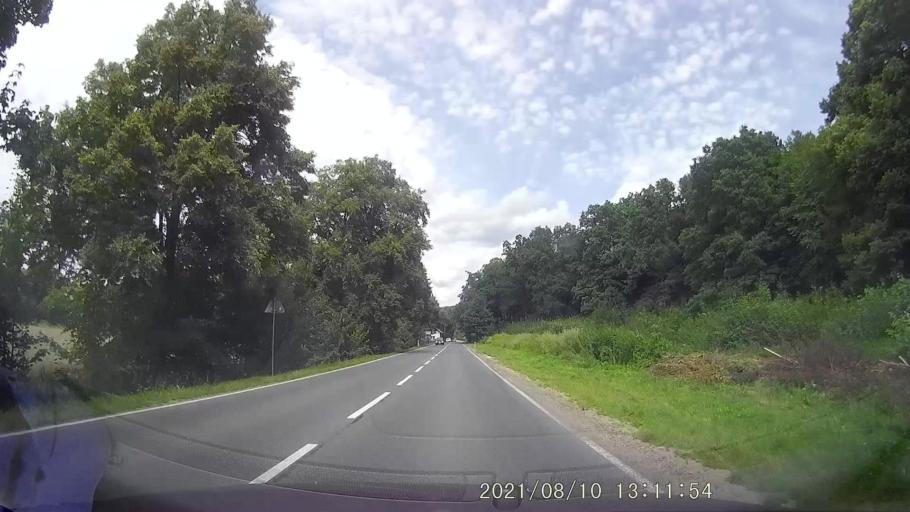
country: PL
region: Lower Silesian Voivodeship
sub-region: Powiat klodzki
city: Bozkow
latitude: 50.5113
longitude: 16.5141
